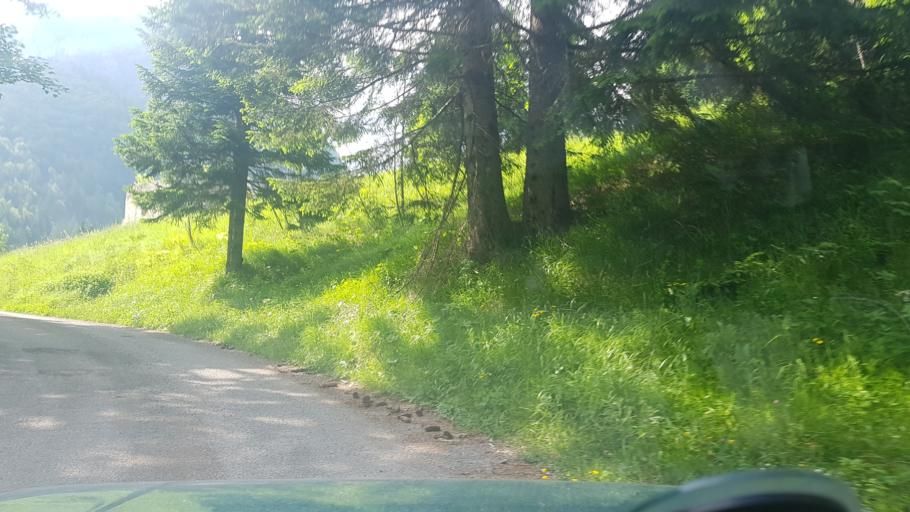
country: IT
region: Friuli Venezia Giulia
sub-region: Provincia di Udine
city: Paularo
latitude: 46.5279
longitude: 13.2137
